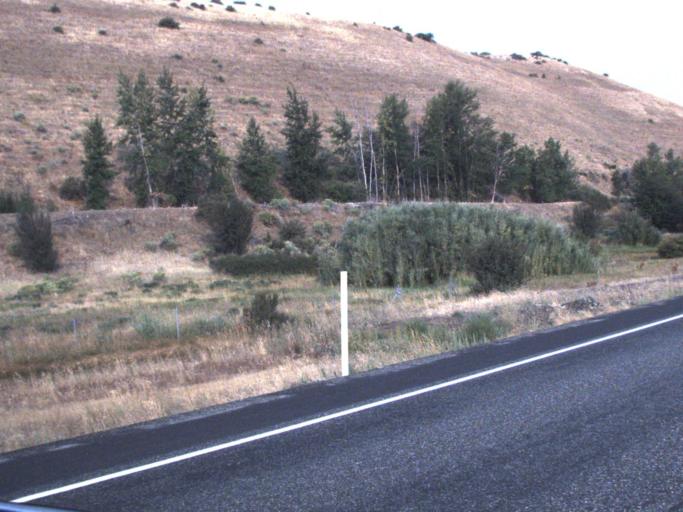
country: US
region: Washington
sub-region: Kittitas County
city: Ellensburg
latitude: 47.0540
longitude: -120.6148
